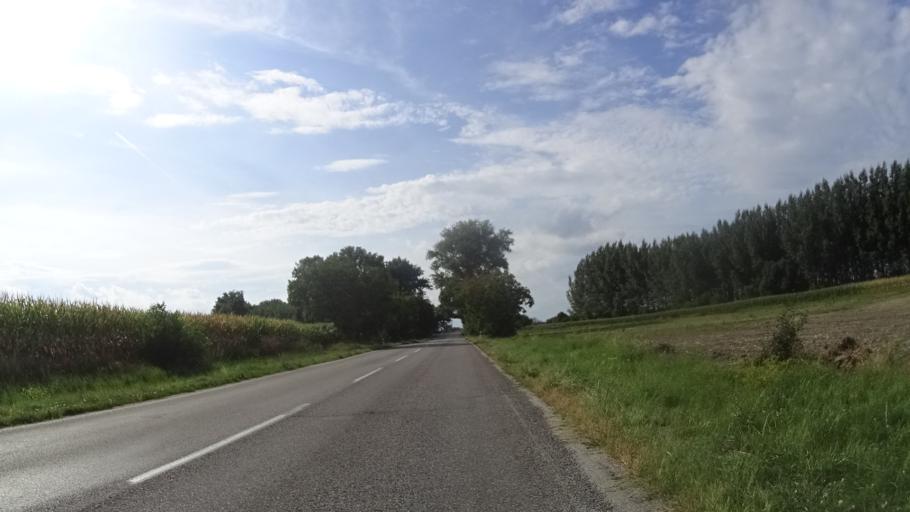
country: SK
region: Trnavsky
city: Gabcikovo
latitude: 47.9268
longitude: 17.4901
